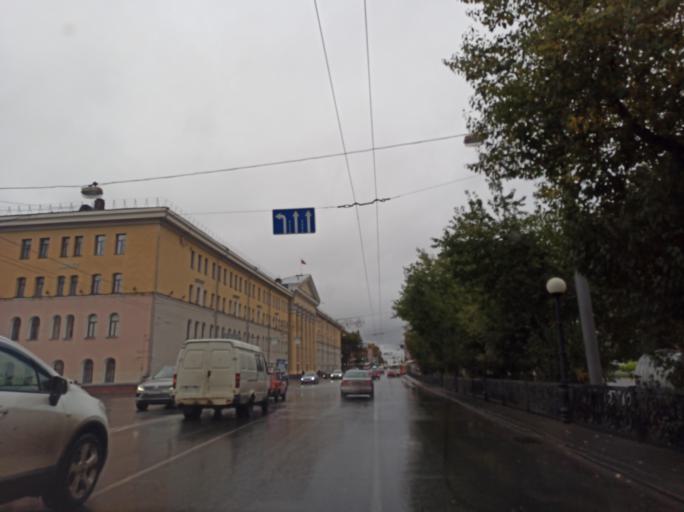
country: RU
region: Tomsk
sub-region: Tomskiy Rayon
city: Tomsk
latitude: 56.4729
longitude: 84.9505
